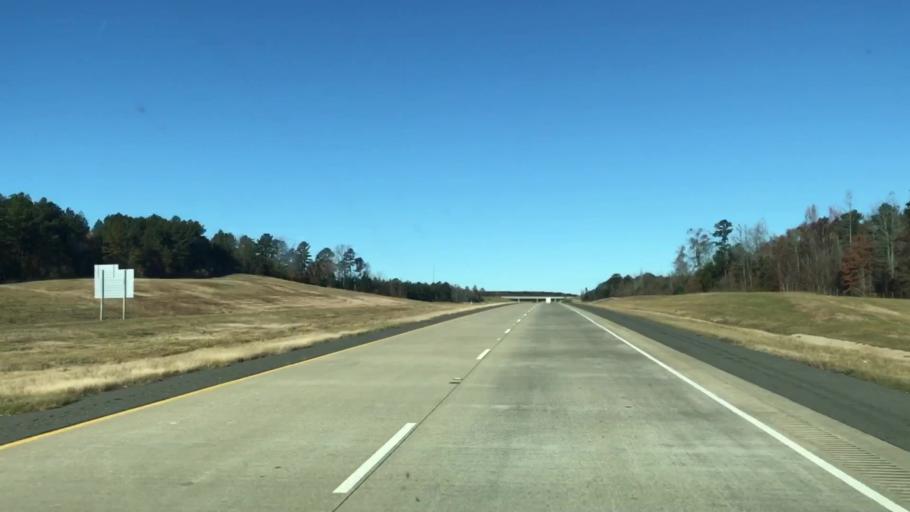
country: US
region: Louisiana
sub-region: Caddo Parish
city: Vivian
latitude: 32.9137
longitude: -93.8747
